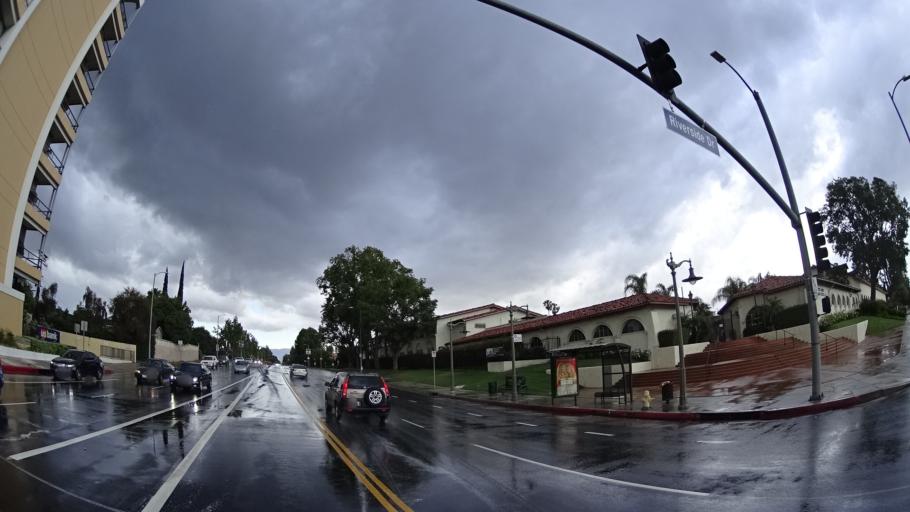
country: US
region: California
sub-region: Los Angeles County
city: Sherman Oaks
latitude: 34.1578
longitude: -118.4313
